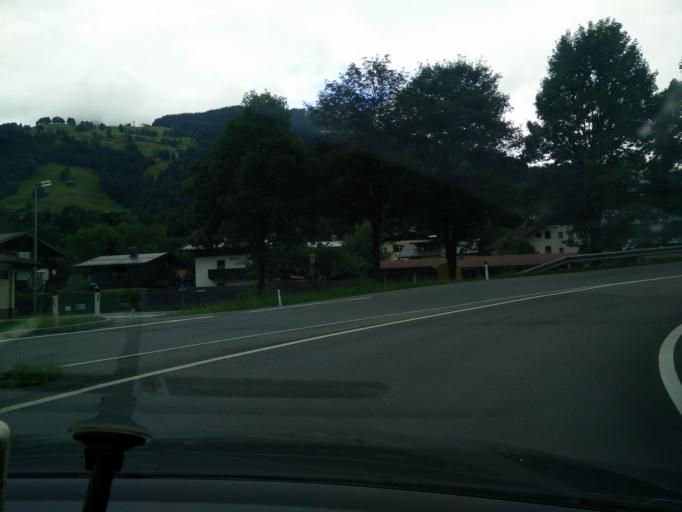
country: AT
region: Tyrol
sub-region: Politischer Bezirk Kitzbuhel
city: Kitzbuhel
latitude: 47.4545
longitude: 12.3876
